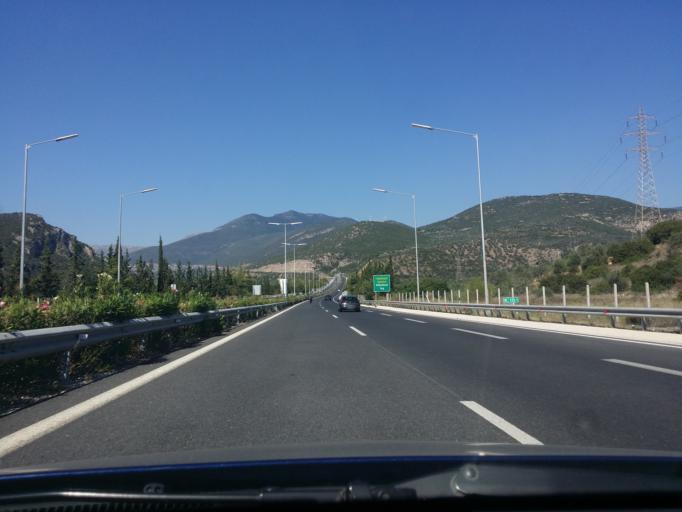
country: GR
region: Peloponnese
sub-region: Nomos Korinthias
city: Nemea
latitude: 37.7207
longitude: 22.5938
